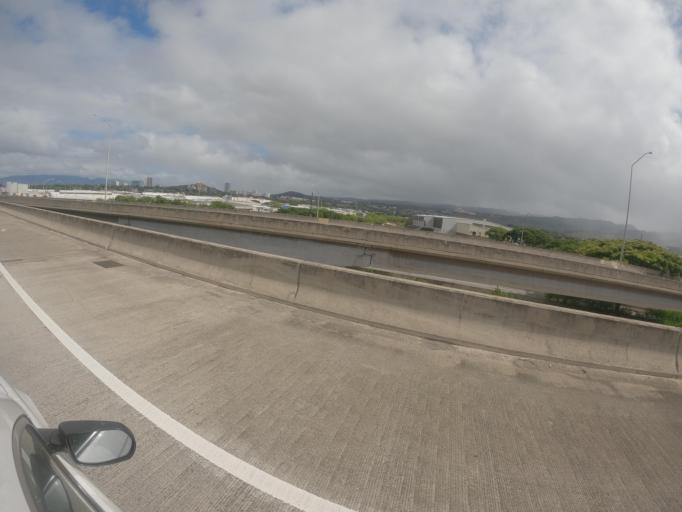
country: US
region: Hawaii
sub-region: Honolulu County
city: Honolulu
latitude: 21.3345
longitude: -157.8929
